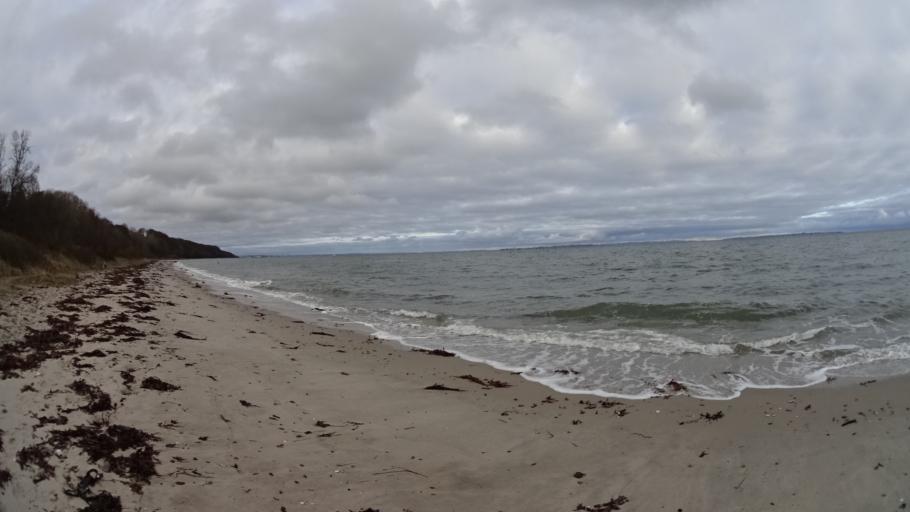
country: DK
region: Central Jutland
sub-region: Arhus Kommune
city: Beder
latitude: 56.0561
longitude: 10.2632
